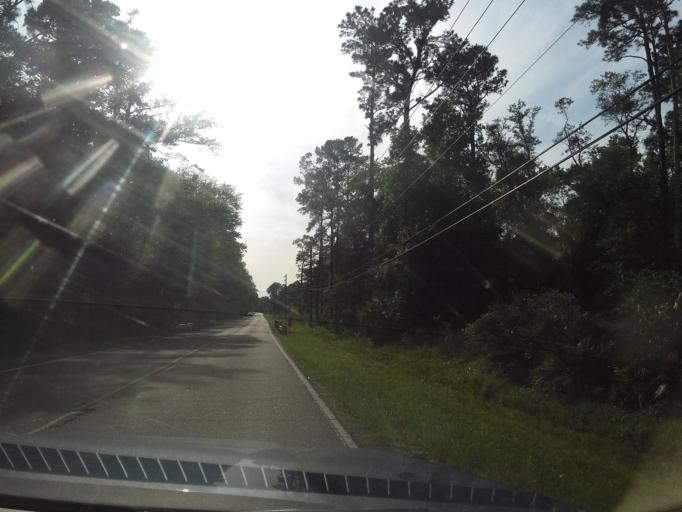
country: US
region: Florida
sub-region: Duval County
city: Jacksonville
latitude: 30.4638
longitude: -81.5457
